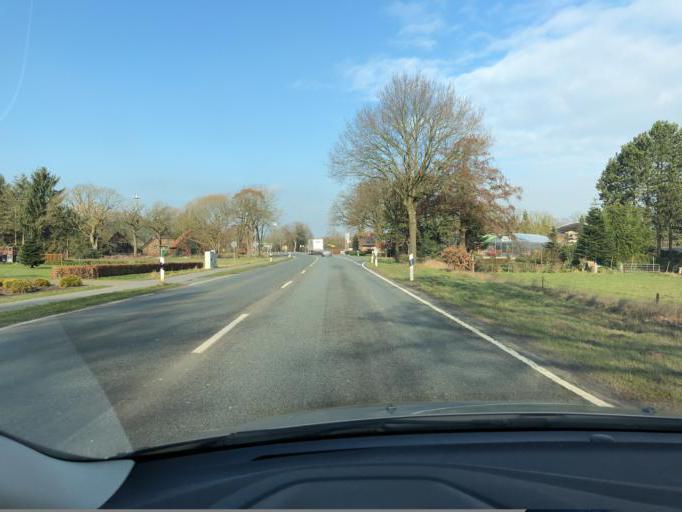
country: DE
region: Lower Saxony
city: Westerstede
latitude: 53.2844
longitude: 7.8978
